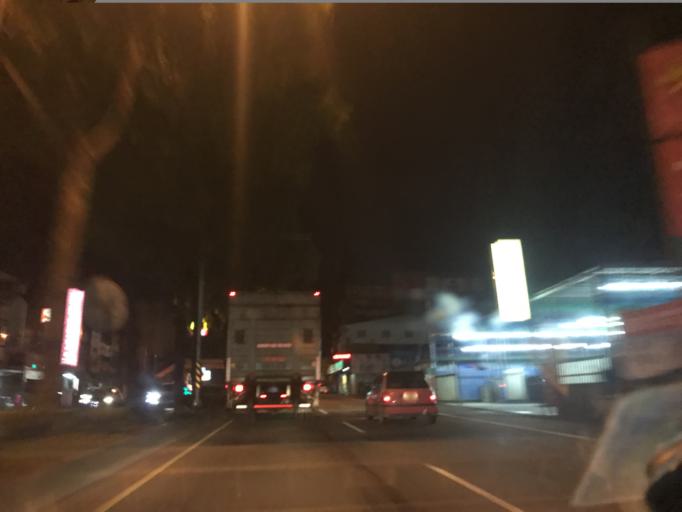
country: TW
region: Taiwan
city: Daxi
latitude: 24.8824
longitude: 121.2118
